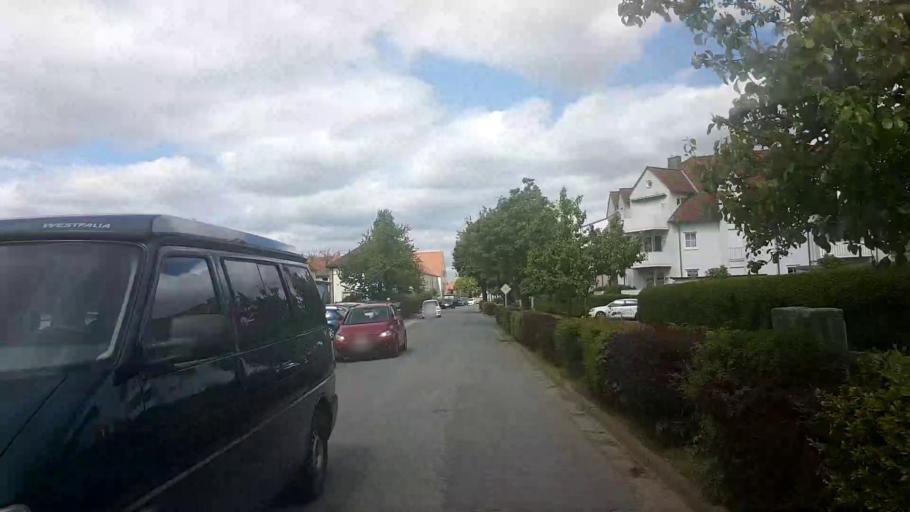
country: DE
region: Bavaria
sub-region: Upper Franconia
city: Bad Staffelstein
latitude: 50.1002
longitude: 11.0041
